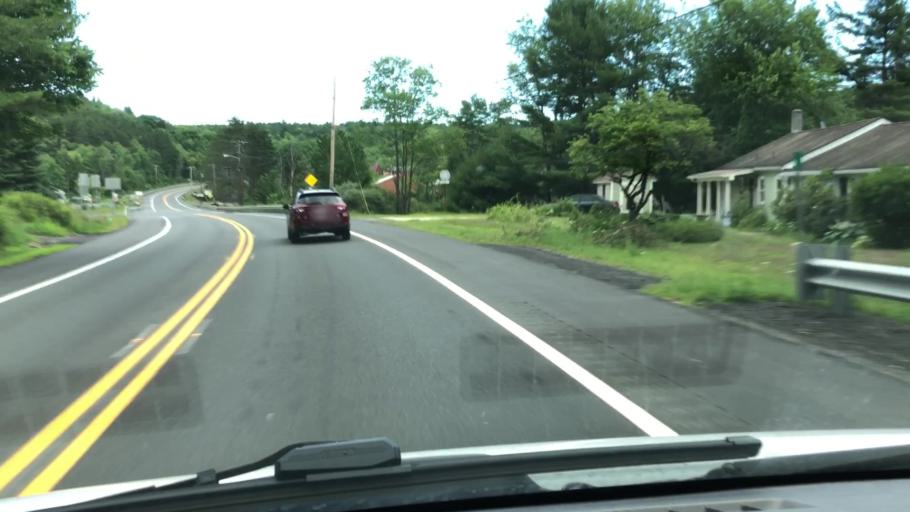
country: US
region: Massachusetts
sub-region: Hampshire County
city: Chesterfield
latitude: 42.4556
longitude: -72.8359
